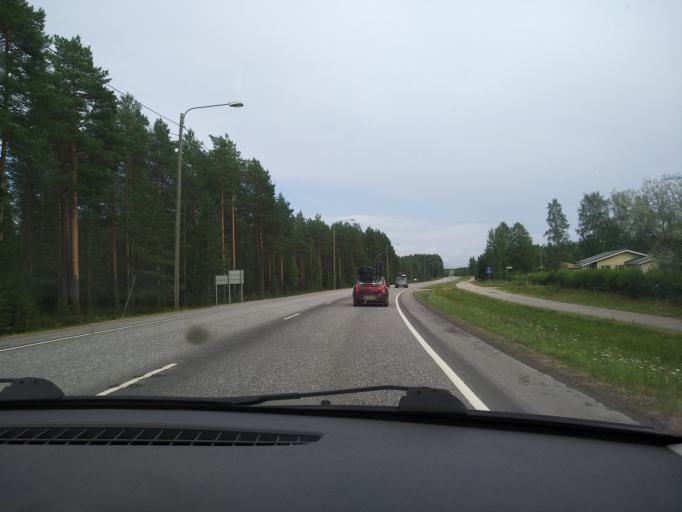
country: FI
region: Kainuu
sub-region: Kajaani
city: Paltamo
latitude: 64.4041
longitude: 27.8620
